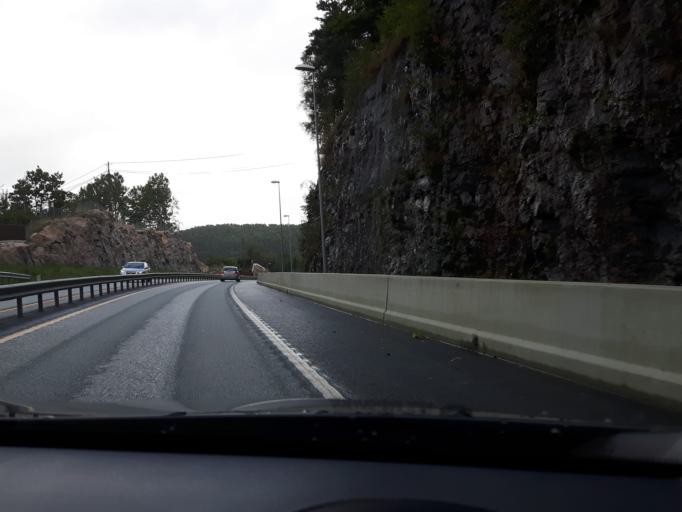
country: NO
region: Vest-Agder
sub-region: Songdalen
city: Nodeland
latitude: 58.1236
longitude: 7.8470
